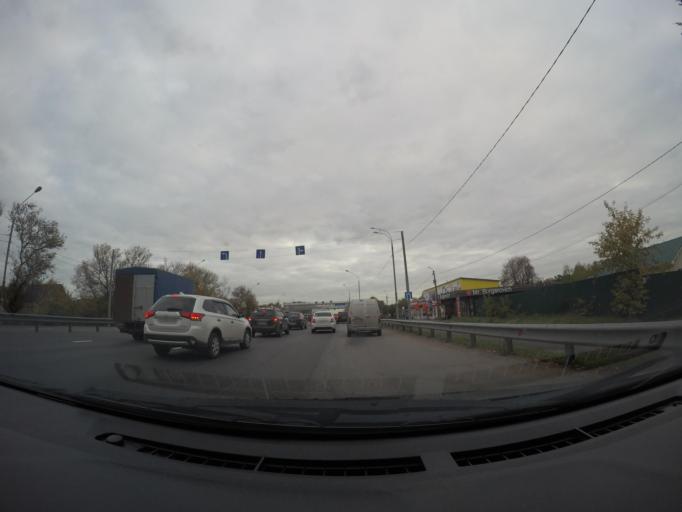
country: RU
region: Moskovskaya
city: Vishnyakovskiye Dachi
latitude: 55.8126
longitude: 38.1057
